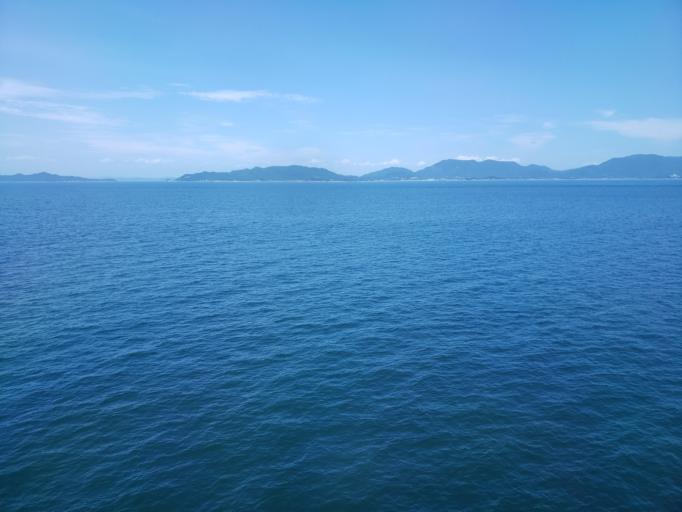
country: JP
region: Kagawa
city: Tonosho
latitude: 34.4062
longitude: 134.1697
